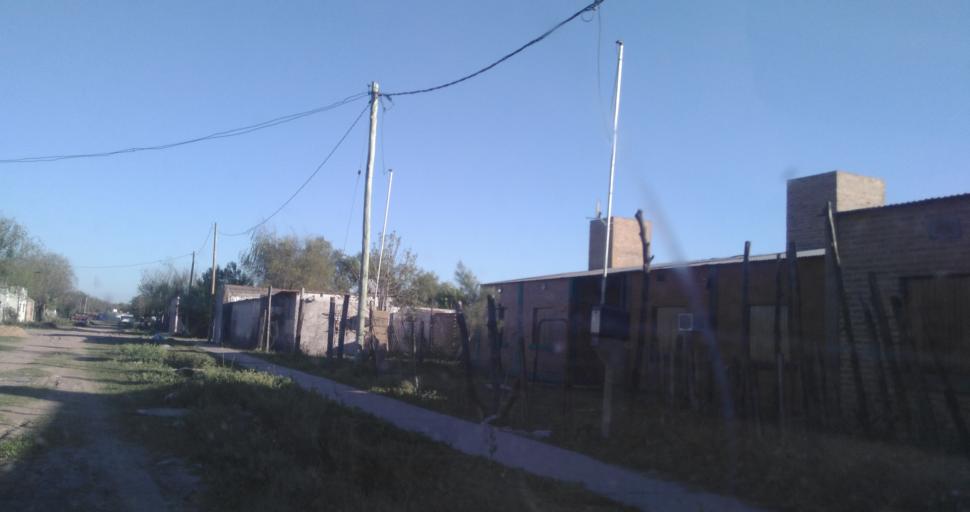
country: AR
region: Chaco
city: Resistencia
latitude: -27.4728
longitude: -59.0168
